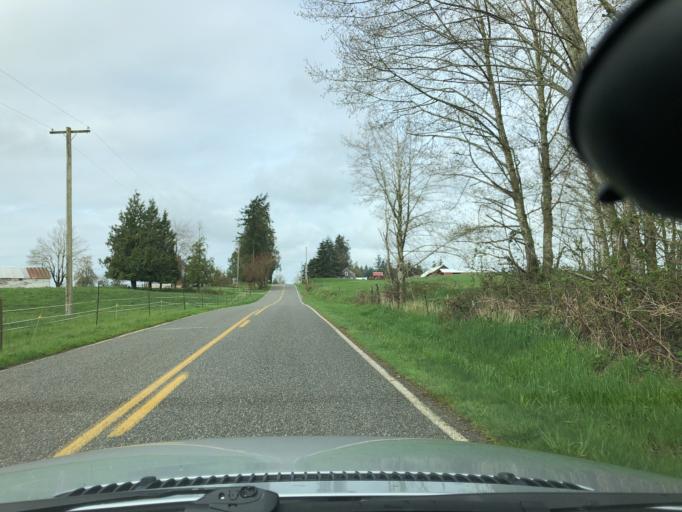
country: US
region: Washington
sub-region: Whatcom County
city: Lynden
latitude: 48.9832
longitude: -122.5386
